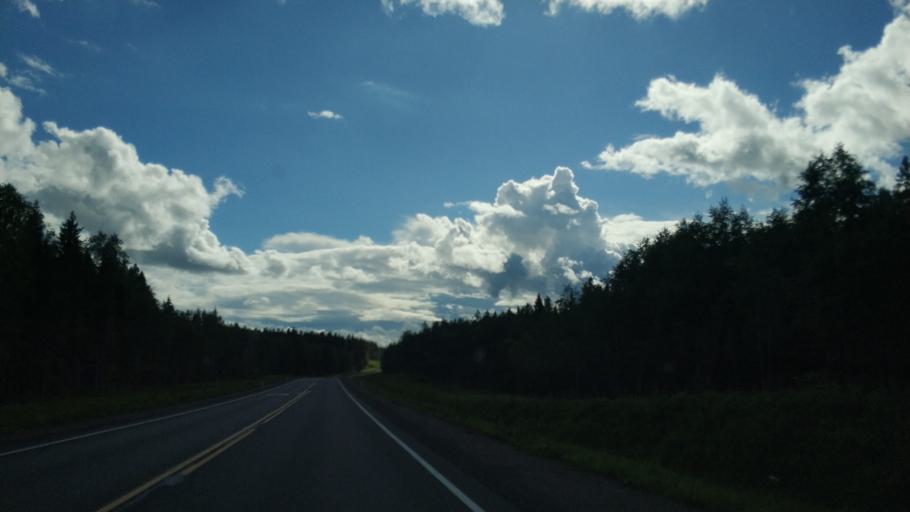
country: RU
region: Republic of Karelia
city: Ruskeala
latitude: 61.8594
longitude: 30.6521
